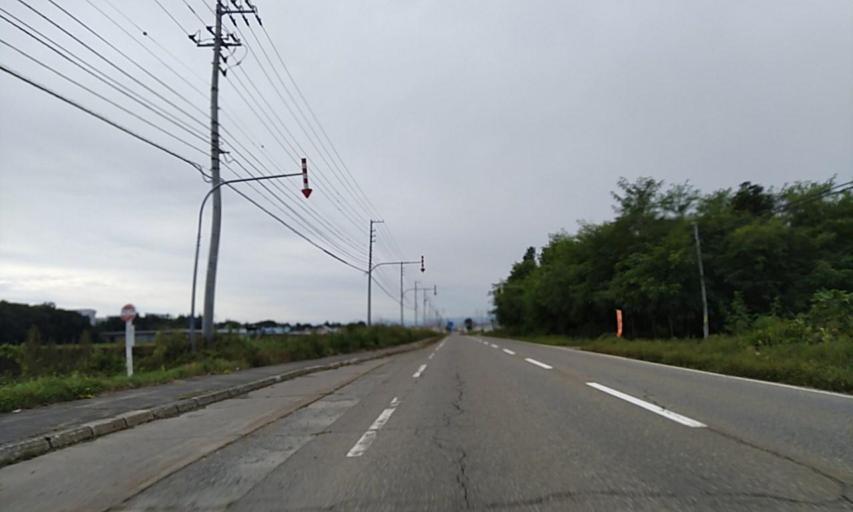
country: JP
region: Hokkaido
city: Obihiro
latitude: 42.7994
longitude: 143.1690
